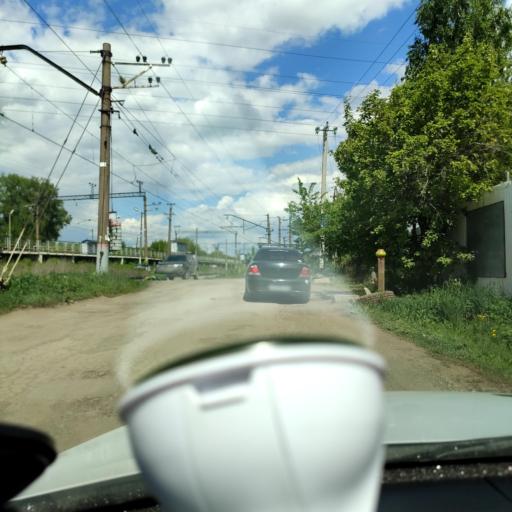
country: RU
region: Samara
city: Petra-Dubrava
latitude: 53.2694
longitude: 50.3174
